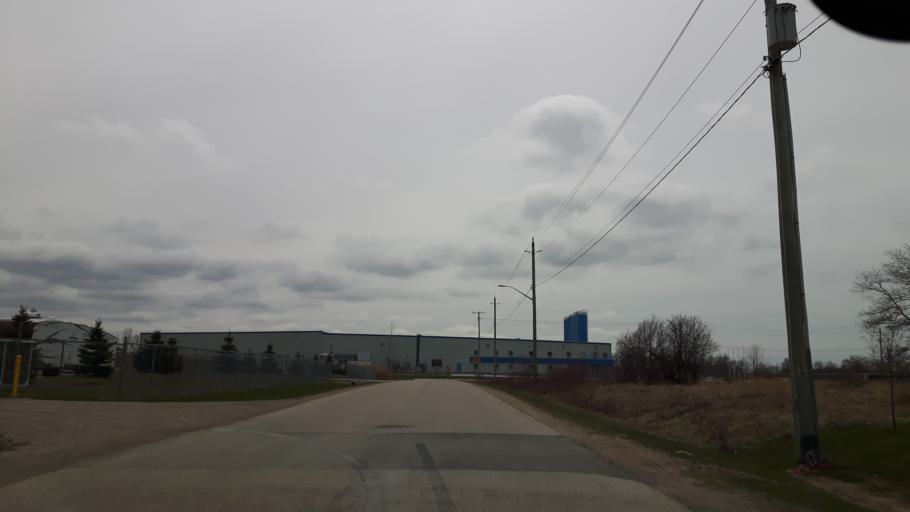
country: CA
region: Ontario
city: Goderich
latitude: 43.7239
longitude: -81.7030
